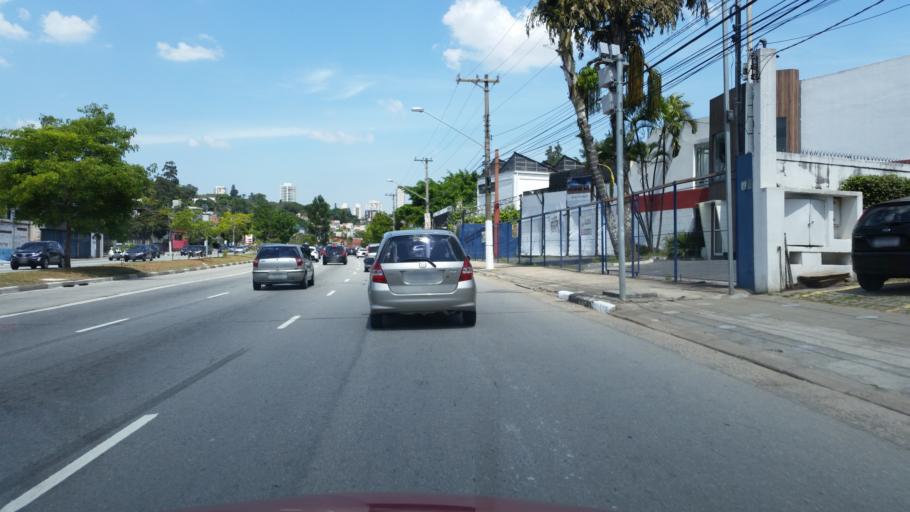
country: BR
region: Sao Paulo
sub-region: Diadema
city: Diadema
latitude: -23.6320
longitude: -46.6825
